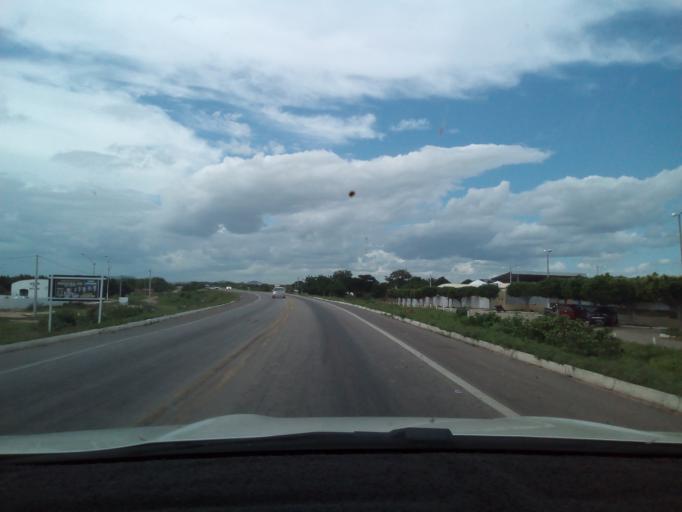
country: BR
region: Rio Grande do Norte
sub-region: Cerro Cora
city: Monte Alegre
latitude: -5.7049
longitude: -36.2500
